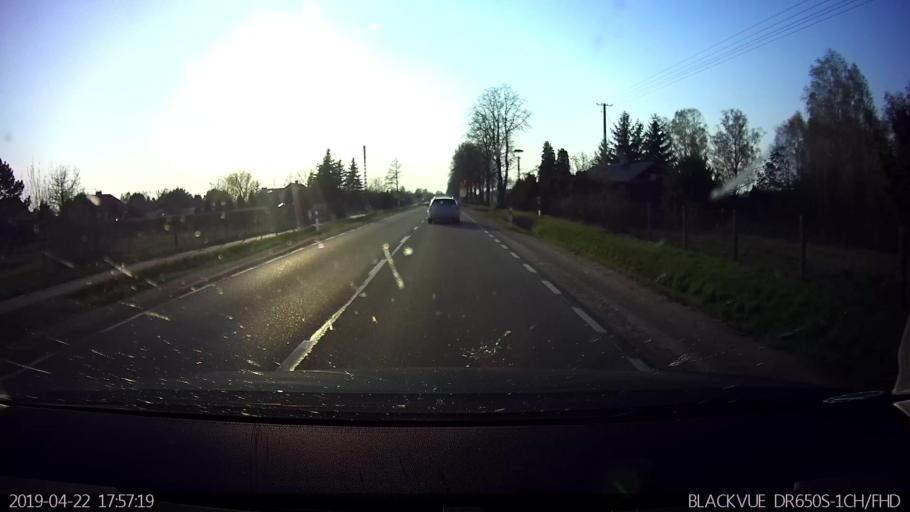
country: PL
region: Masovian Voivodeship
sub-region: Powiat wegrowski
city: Korytnica
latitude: 52.4683
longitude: 21.8938
